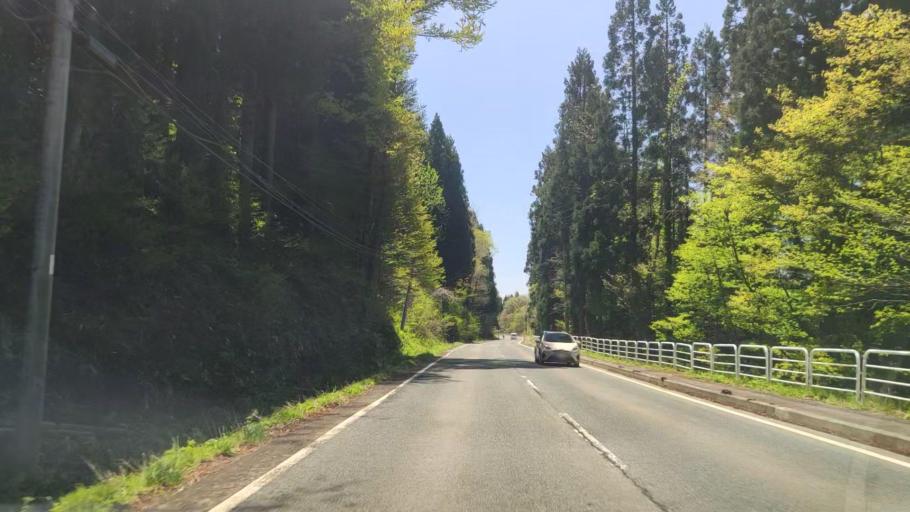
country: JP
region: Yamagata
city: Shinjo
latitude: 38.8945
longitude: 140.3249
